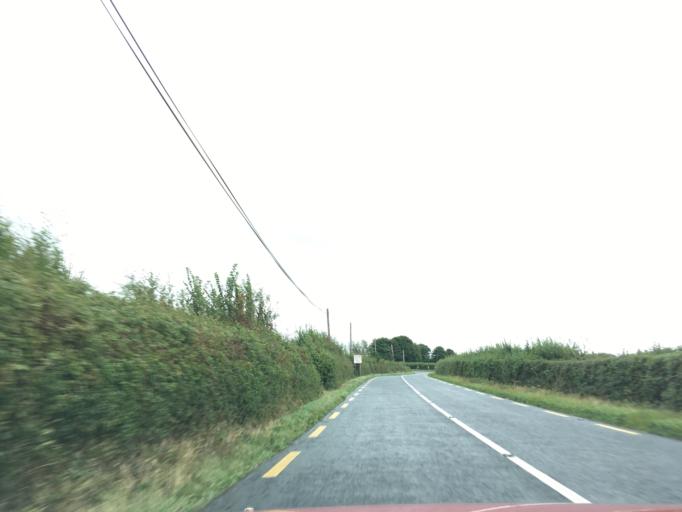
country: IE
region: Munster
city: Fethard
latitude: 52.4215
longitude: -7.7698
